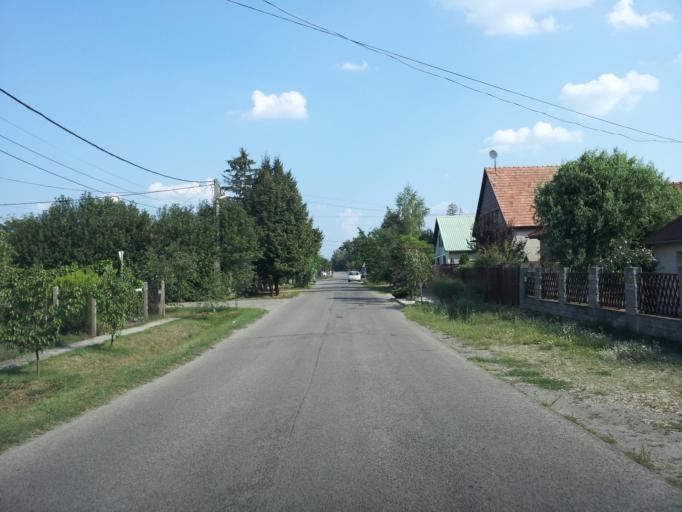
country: HU
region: Pest
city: Szigethalom
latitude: 47.3162
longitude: 19.0026
